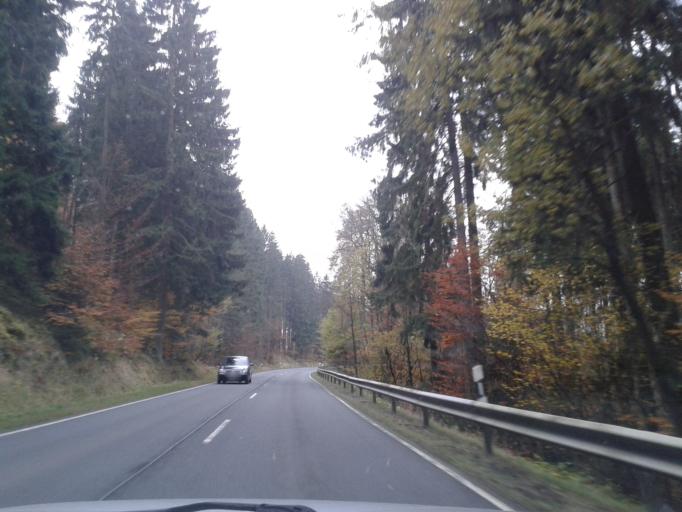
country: DE
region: North Rhine-Westphalia
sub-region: Regierungsbezirk Arnsberg
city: Erndtebruck
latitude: 50.9838
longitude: 8.3392
